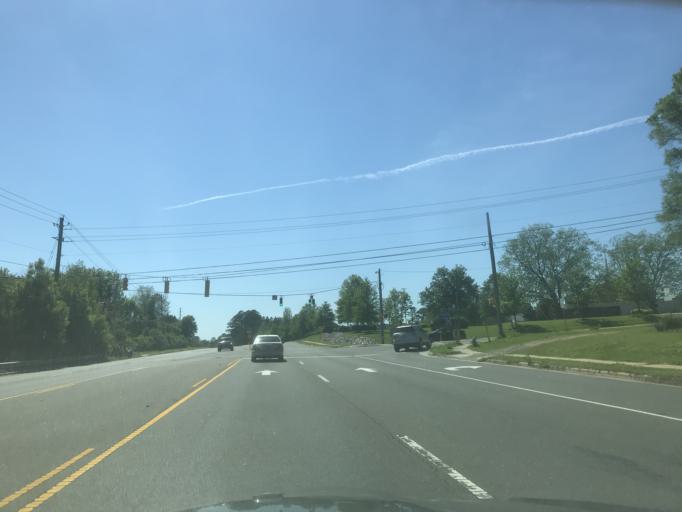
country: US
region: North Carolina
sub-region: Wake County
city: West Raleigh
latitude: 35.7486
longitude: -78.7204
